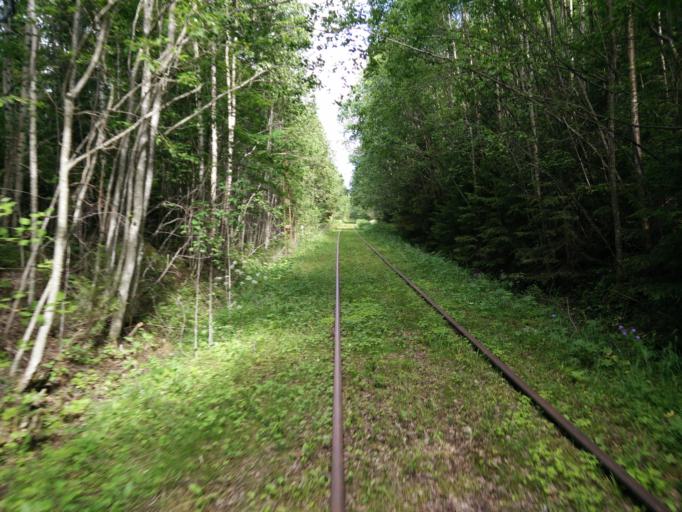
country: SE
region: Gaevleborg
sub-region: Hudiksvalls Kommun
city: Delsbo
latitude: 61.8003
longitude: 16.4001
